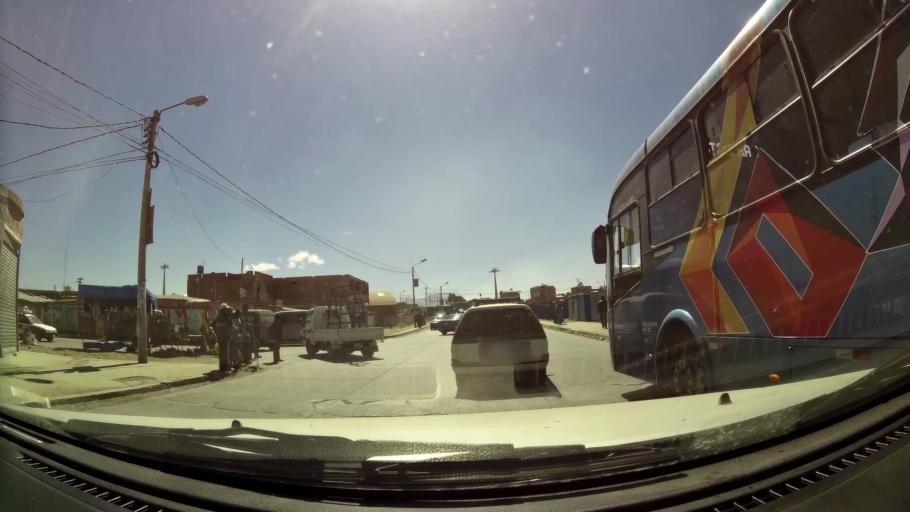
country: BO
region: La Paz
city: La Paz
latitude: -16.4925
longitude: -68.2035
